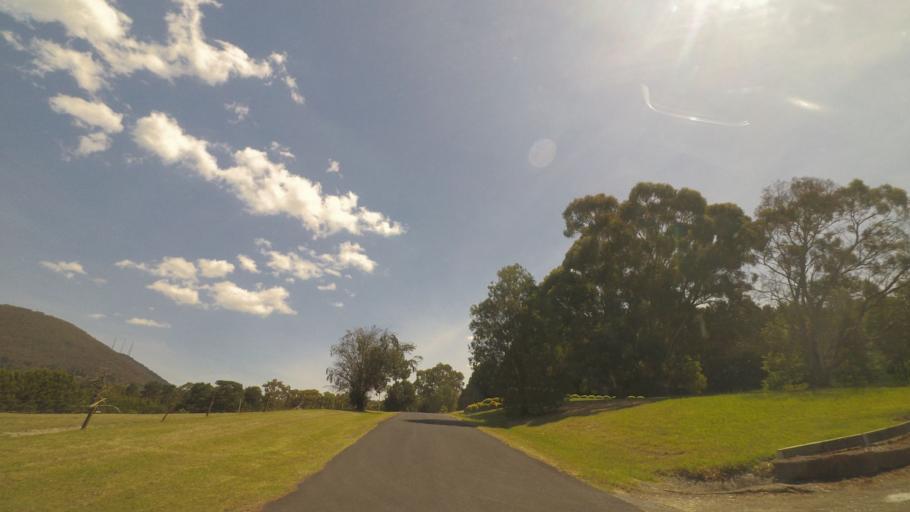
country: AU
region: Victoria
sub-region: Yarra Ranges
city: Montrose
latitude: -37.8027
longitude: 145.3515
